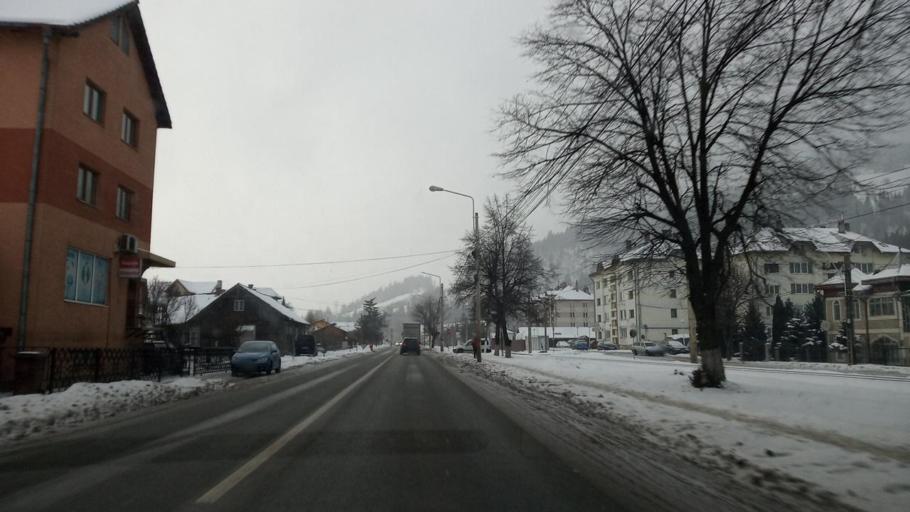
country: RO
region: Suceava
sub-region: Municipiul Vatra Dornei
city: Vatra Dornei
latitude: 47.3478
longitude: 25.3398
